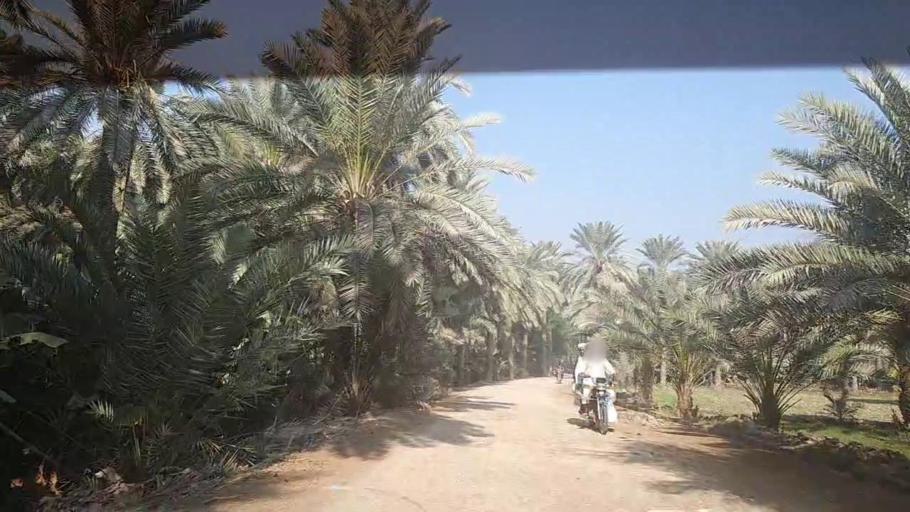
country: PK
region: Sindh
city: Khairpur
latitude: 27.4648
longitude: 68.7172
